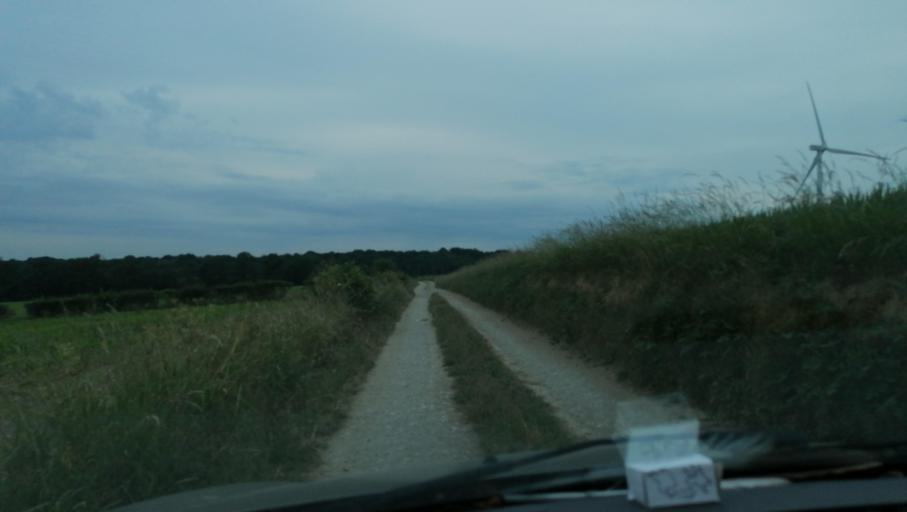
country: BE
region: Wallonia
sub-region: Province du Hainaut
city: Beaumont
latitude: 50.2079
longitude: 4.1623
